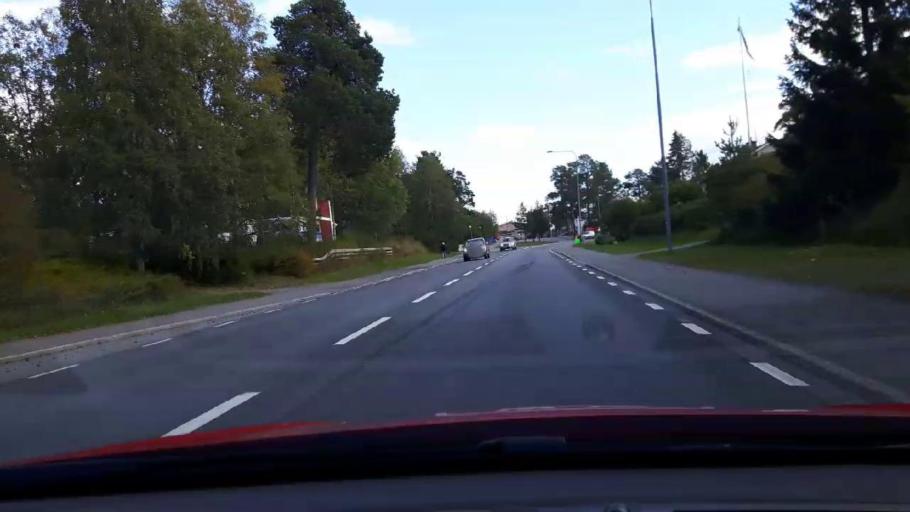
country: SE
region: Jaemtland
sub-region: OEstersunds Kommun
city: Brunflo
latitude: 63.0836
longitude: 14.8195
